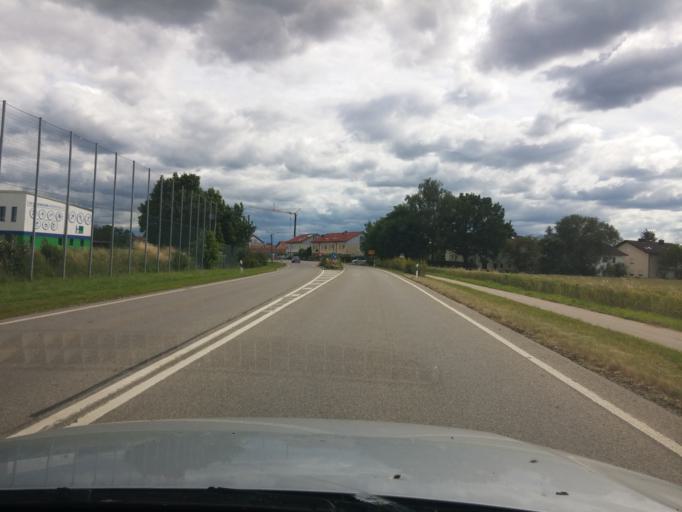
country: DE
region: Bavaria
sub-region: Upper Bavaria
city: Hohenbrunn
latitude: 48.0530
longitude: 11.7049
